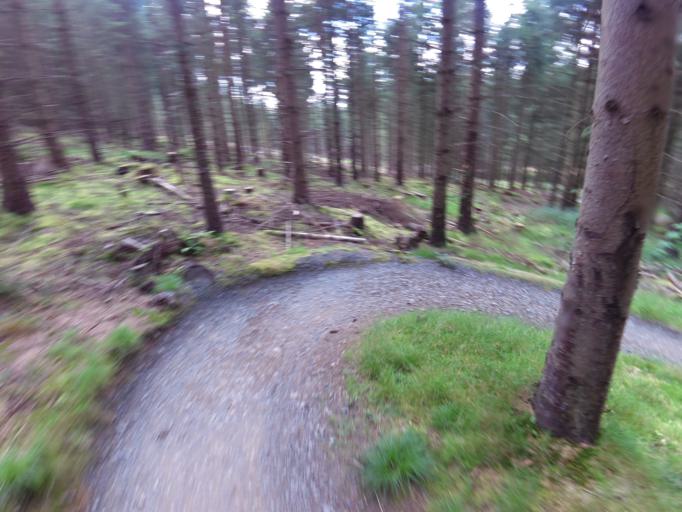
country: GB
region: Scotland
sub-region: The Scottish Borders
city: Peebles
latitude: 55.6585
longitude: -3.1310
